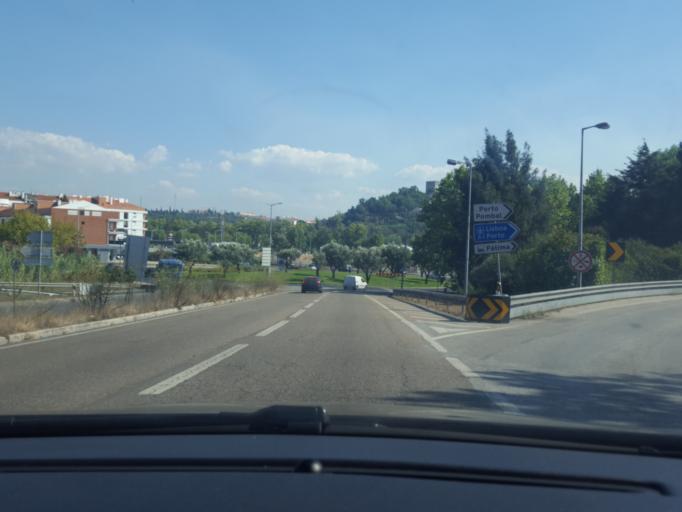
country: PT
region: Leiria
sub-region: Leiria
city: Leiria
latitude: 39.7540
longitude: -8.8152
